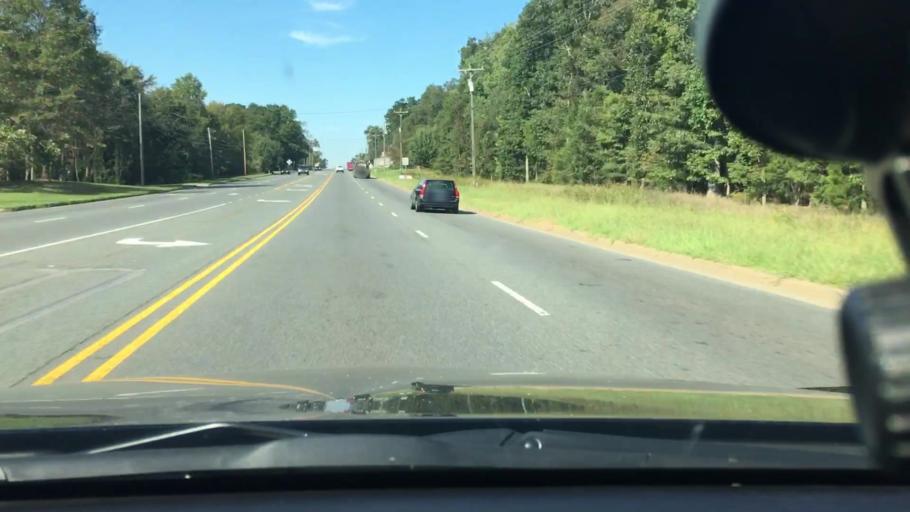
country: US
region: North Carolina
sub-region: Cabarrus County
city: Midland
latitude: 35.2496
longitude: -80.5390
